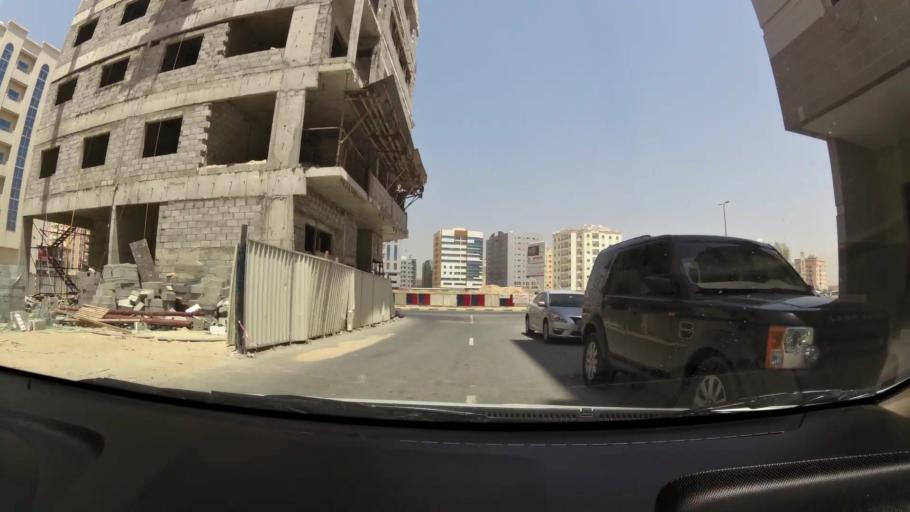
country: AE
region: Ajman
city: Ajman
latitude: 25.4075
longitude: 55.5140
